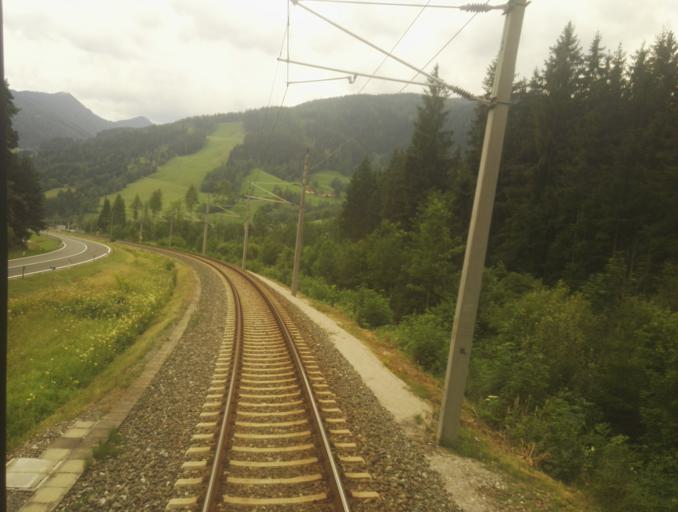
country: AT
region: Salzburg
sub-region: Politischer Bezirk Sankt Johann im Pongau
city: Forstau
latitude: 47.3940
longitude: 13.5917
